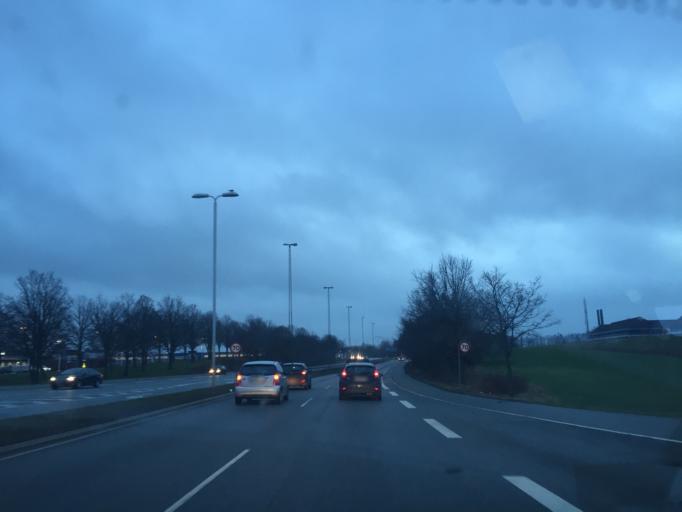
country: DK
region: Capital Region
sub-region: Hoje-Taastrup Kommune
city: Taastrup
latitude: 55.6603
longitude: 12.2824
